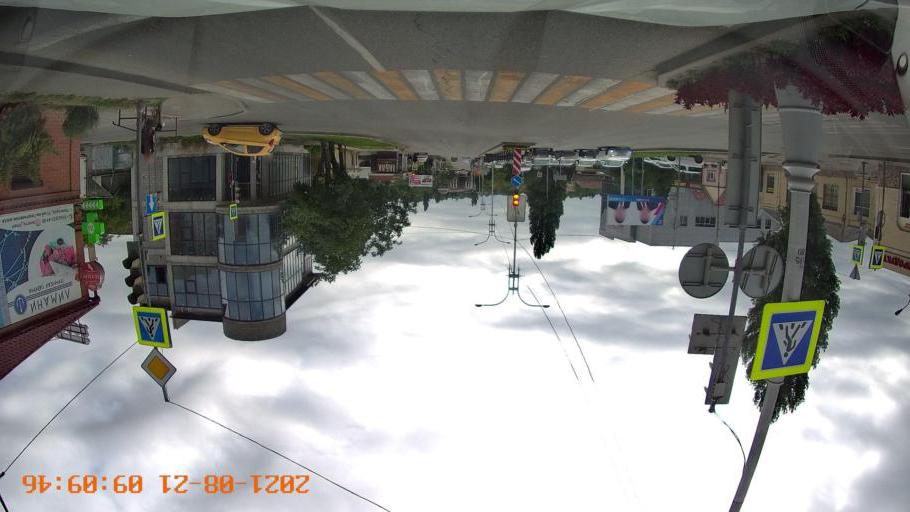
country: RU
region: Stavropol'skiy
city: Goryachevodskiy
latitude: 44.0281
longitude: 43.0730
